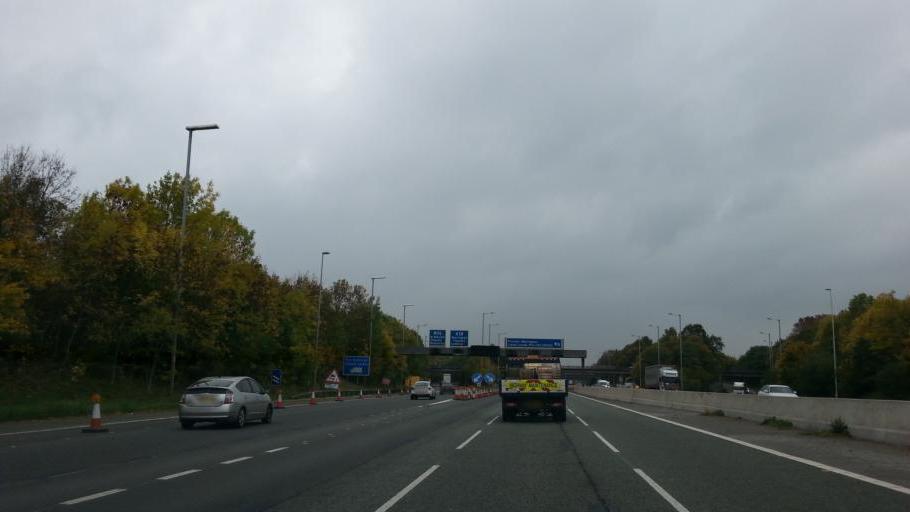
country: GB
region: England
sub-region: Warrington
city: Lymm
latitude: 53.3474
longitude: -2.4976
